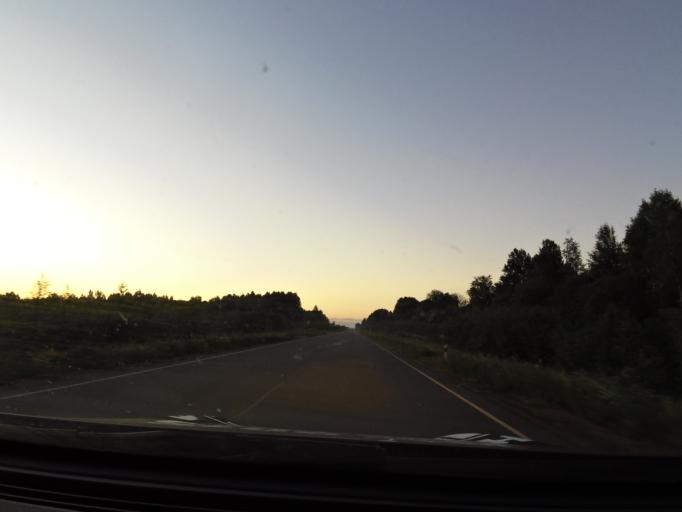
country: RU
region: Vologda
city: Vytegra
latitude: 60.9673
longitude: 36.0915
